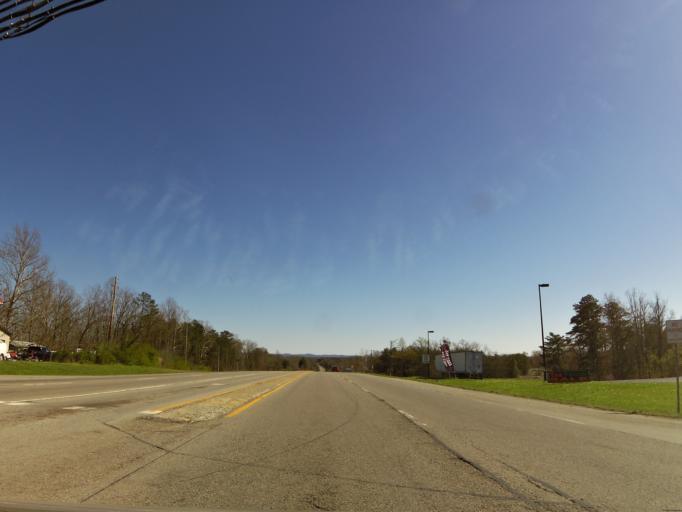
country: US
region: Kentucky
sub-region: McCreary County
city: Whitley City
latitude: 36.7230
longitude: -84.4671
